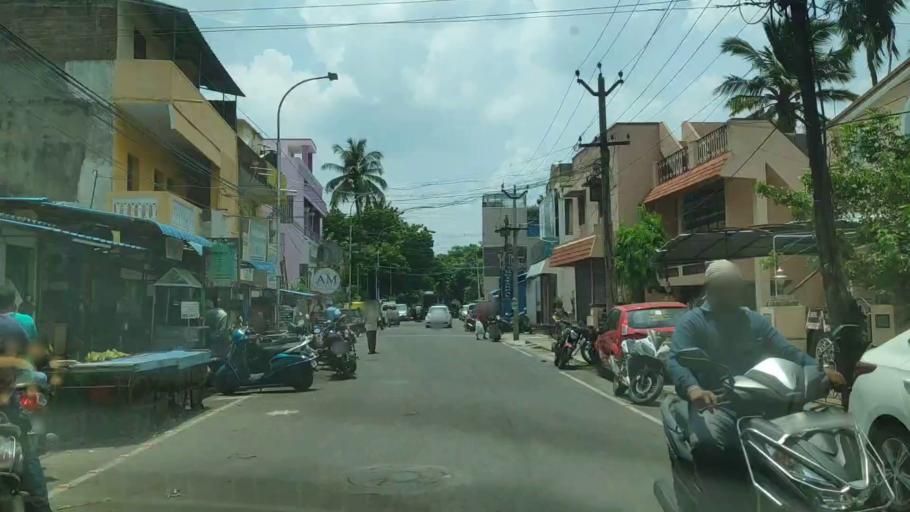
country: IN
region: Tamil Nadu
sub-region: Thiruvallur
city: Ambattur
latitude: 13.1215
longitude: 80.1511
